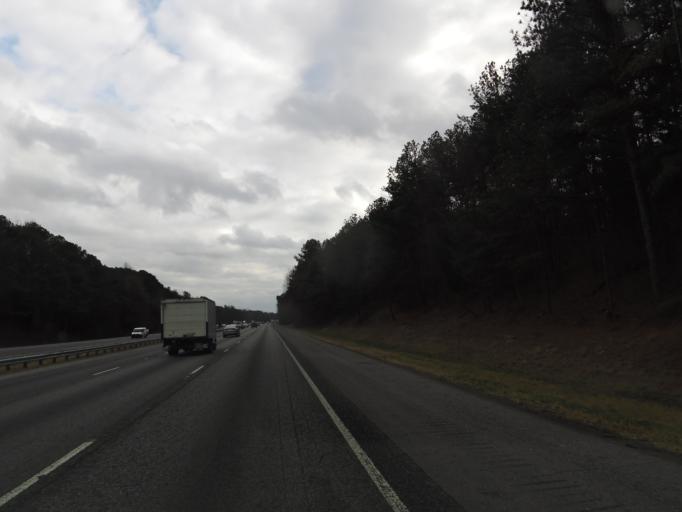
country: US
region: Georgia
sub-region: Gordon County
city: Calhoun
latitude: 34.6074
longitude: -84.9600
